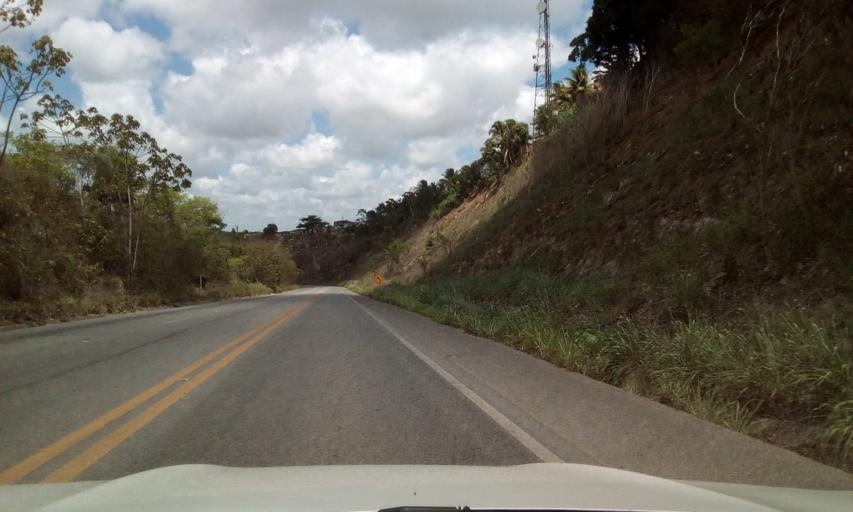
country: BR
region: Alagoas
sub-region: Sao Miguel Dos Campos
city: Sao Miguel dos Campos
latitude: -9.7910
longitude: -36.1065
